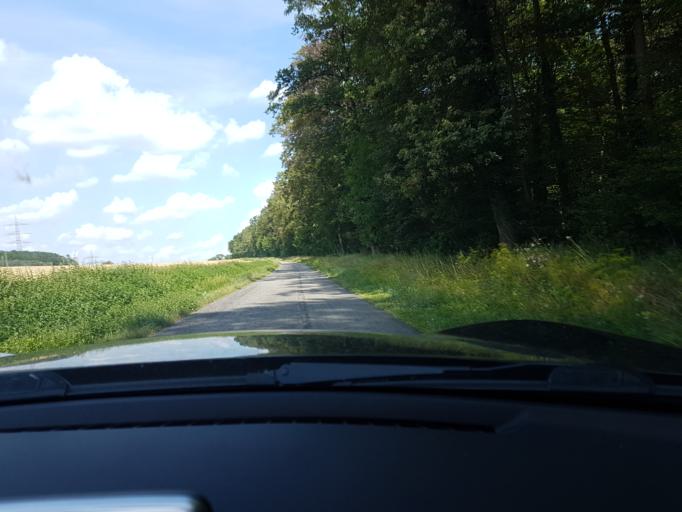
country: DE
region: Baden-Wuerttemberg
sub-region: Karlsruhe Region
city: Neckarzimmern
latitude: 49.3264
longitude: 9.1574
